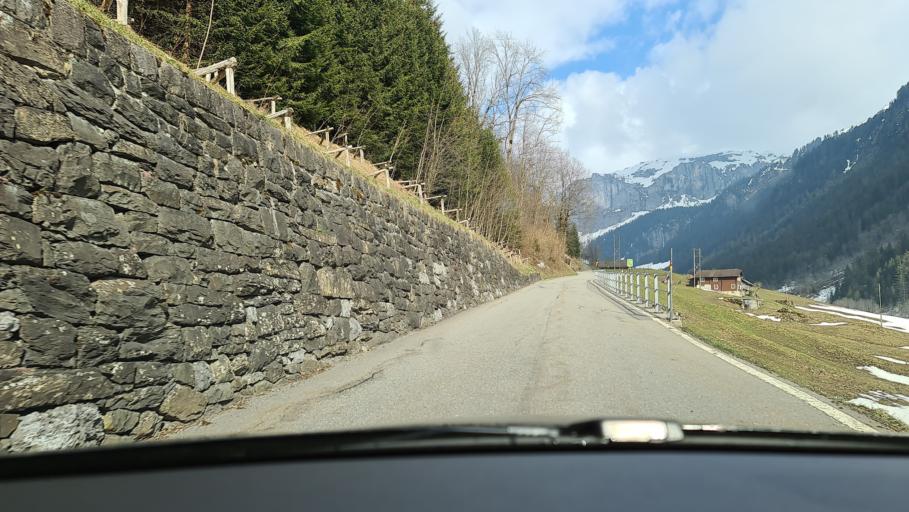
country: CH
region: Schwyz
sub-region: Bezirk Schwyz
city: Muotathal
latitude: 46.8652
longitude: 8.7810
